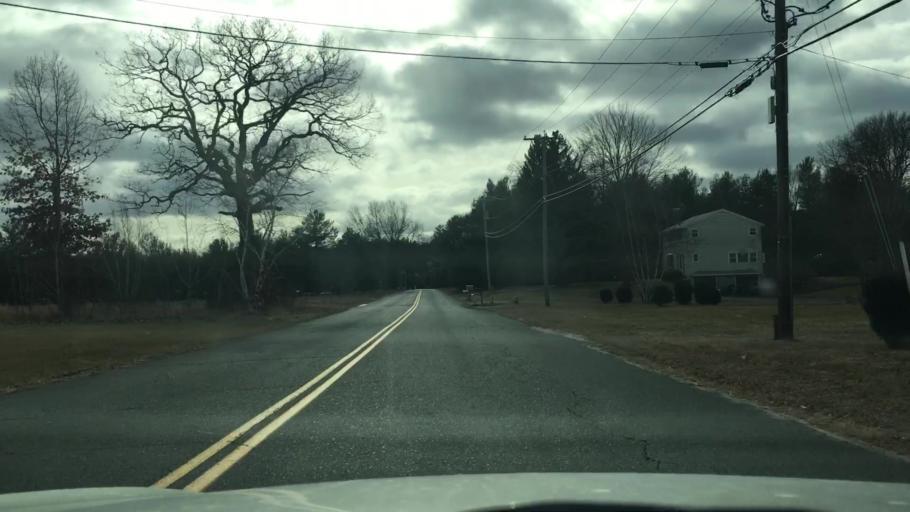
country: US
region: Massachusetts
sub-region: Hampden County
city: Southwick
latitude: 42.0686
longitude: -72.7456
